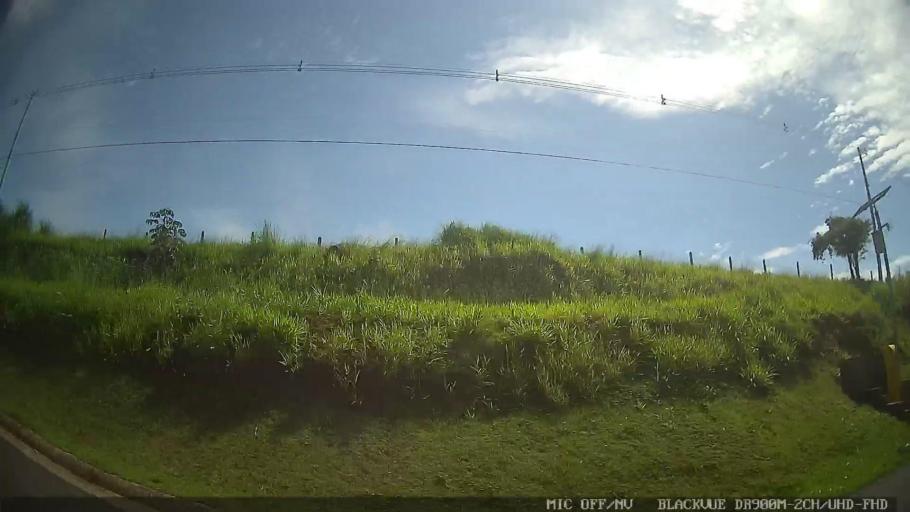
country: BR
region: Sao Paulo
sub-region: Porto Feliz
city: Porto Feliz
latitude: -23.2047
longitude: -47.6004
